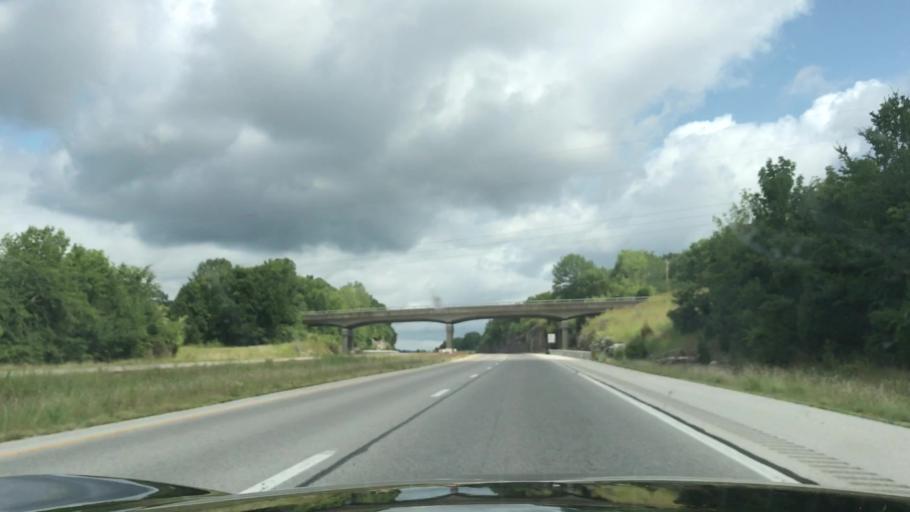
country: US
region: Kentucky
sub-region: Warren County
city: Bowling Green
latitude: 37.0011
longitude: -86.5062
